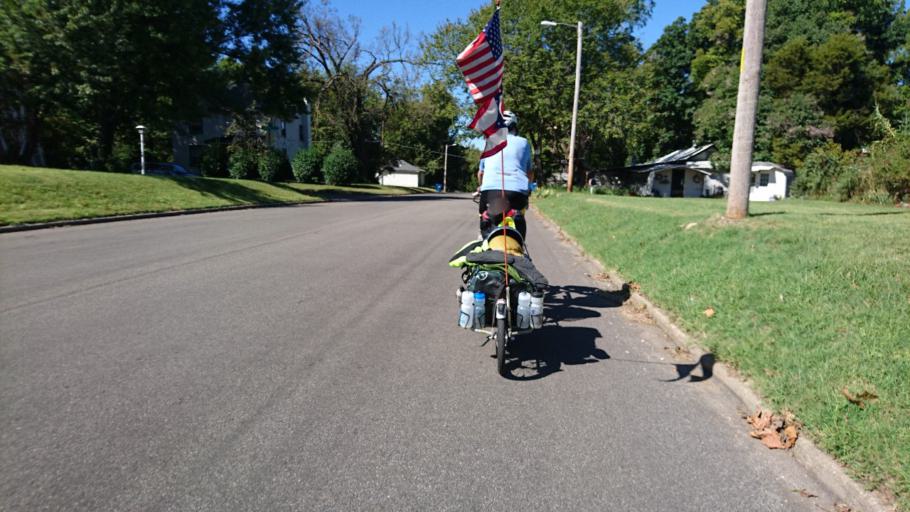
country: US
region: Missouri
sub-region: Jasper County
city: Joplin
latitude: 37.0906
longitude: -94.5450
